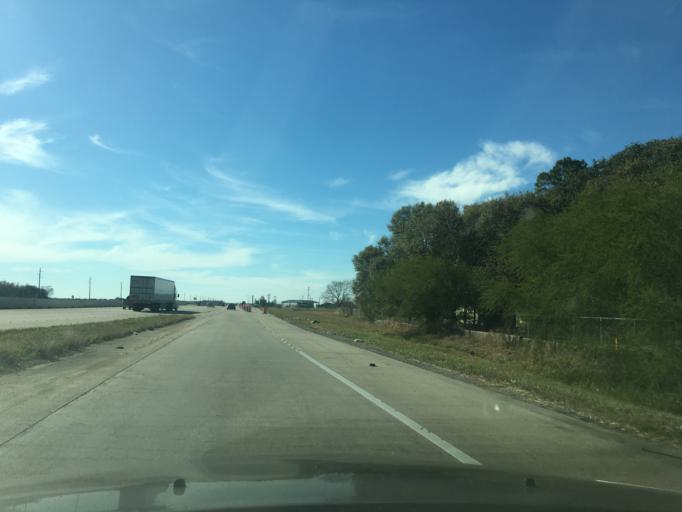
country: US
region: Texas
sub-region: Fort Bend County
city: Pleak
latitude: 29.4928
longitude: -95.9155
